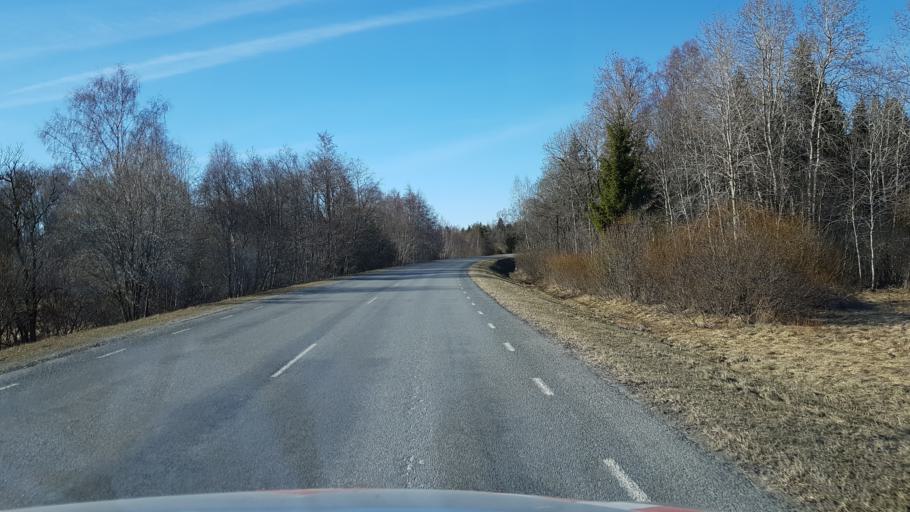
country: EE
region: Harju
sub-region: Keila linn
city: Keila
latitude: 59.2425
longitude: 24.4632
